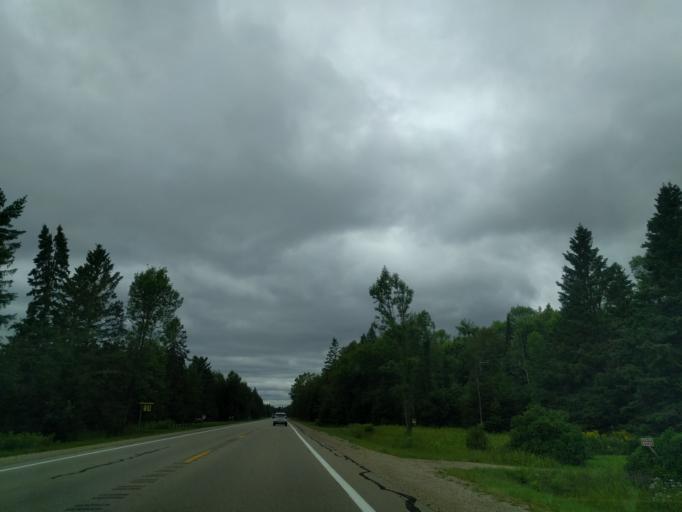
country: US
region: Michigan
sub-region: Delta County
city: Escanaba
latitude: 45.4666
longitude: -87.3194
